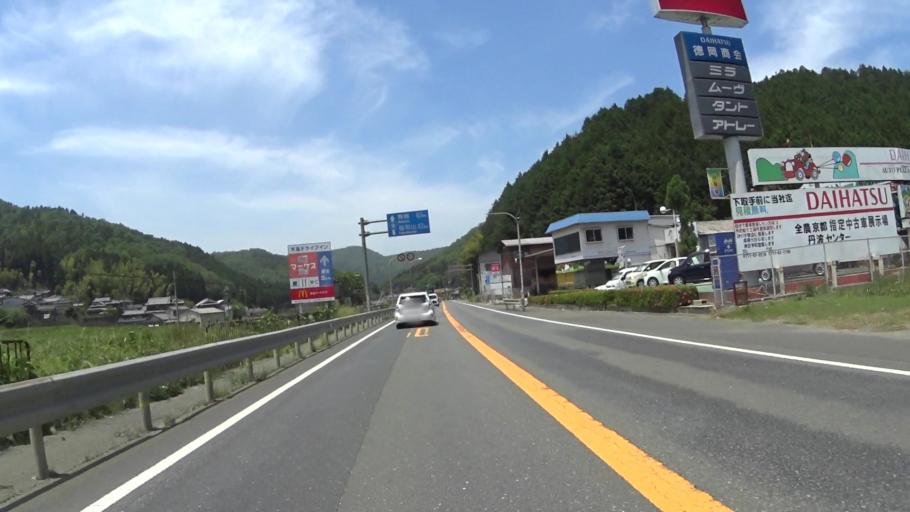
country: JP
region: Kyoto
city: Kameoka
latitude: 35.1316
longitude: 135.4312
